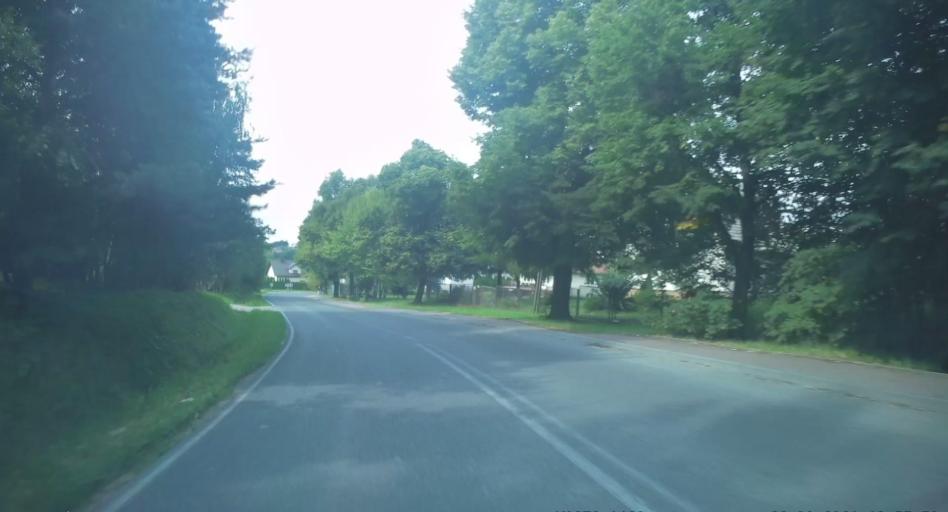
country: PL
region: Lesser Poland Voivodeship
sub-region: Powiat myslenicki
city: Borzeta
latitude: 49.8742
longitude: 19.9885
